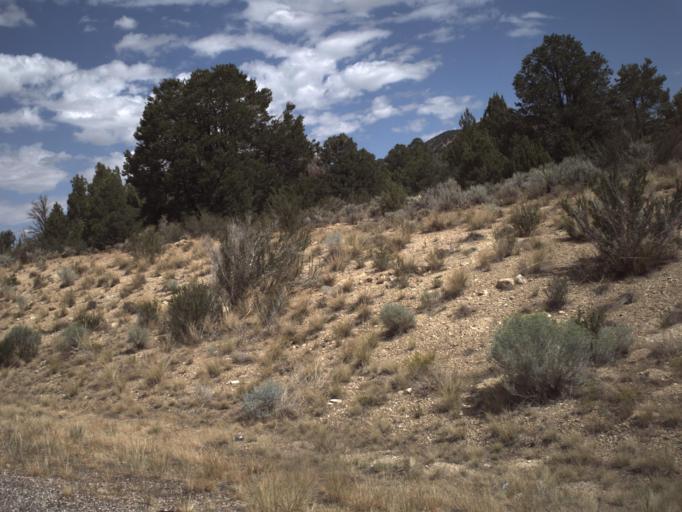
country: US
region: Utah
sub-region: Sanpete County
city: Gunnison
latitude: 39.1618
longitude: -112.0720
